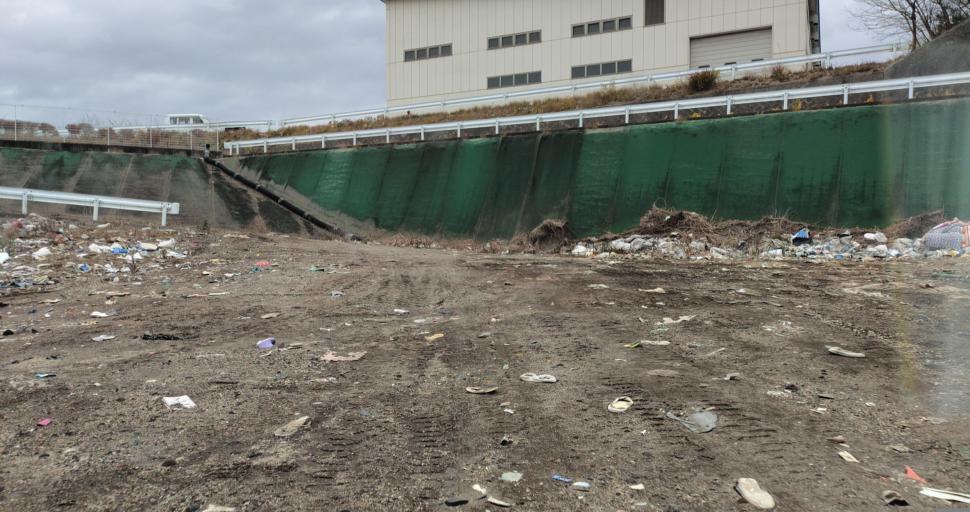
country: JP
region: Nagano
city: Komoro
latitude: 36.2866
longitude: 138.4906
